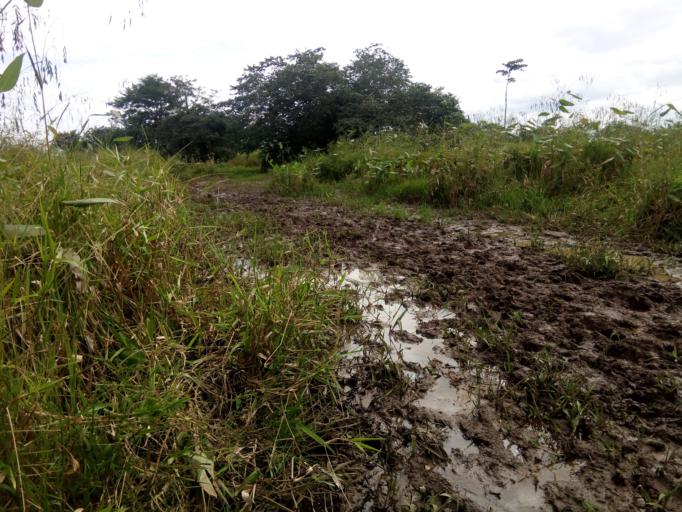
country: CR
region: Alajuela
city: San Jose
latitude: 11.0556
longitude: -85.1926
